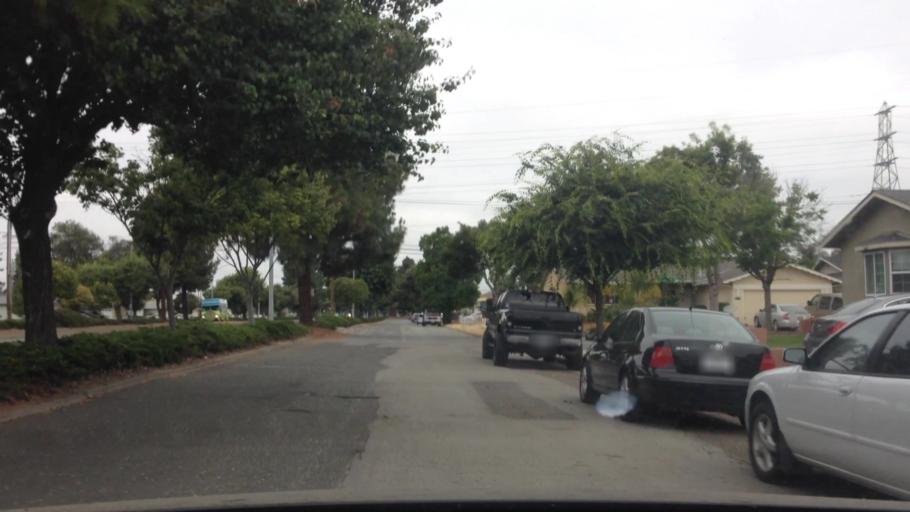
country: US
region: California
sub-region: Alameda County
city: Fremont
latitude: 37.5246
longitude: -121.9750
